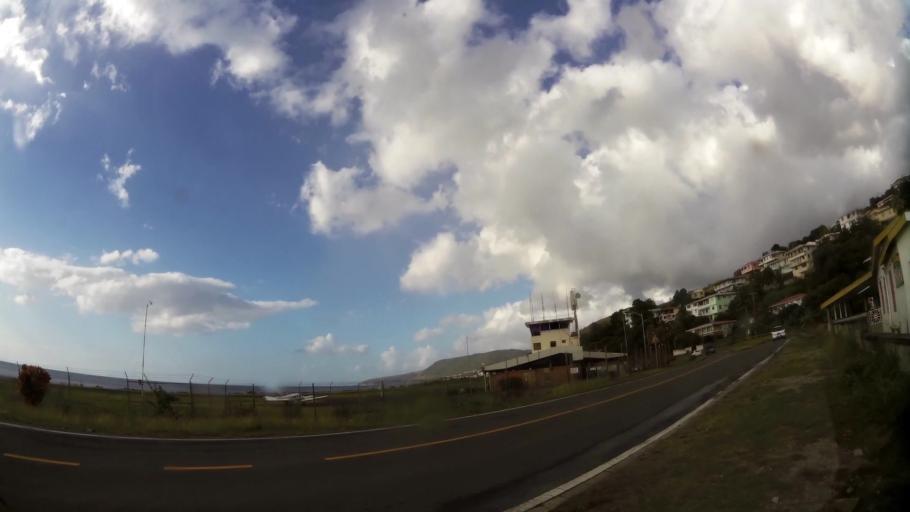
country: DM
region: Saint Paul
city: Mahaut
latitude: 15.3381
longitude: -61.3917
